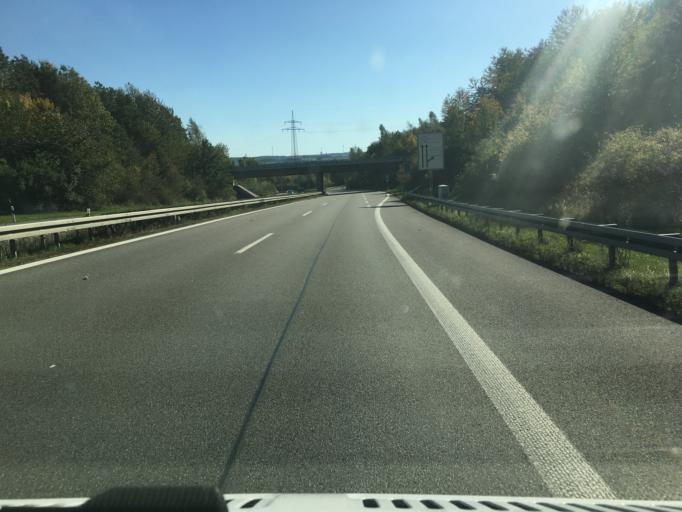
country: DE
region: Saxony
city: Dennheritz
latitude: 50.7895
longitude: 12.4752
